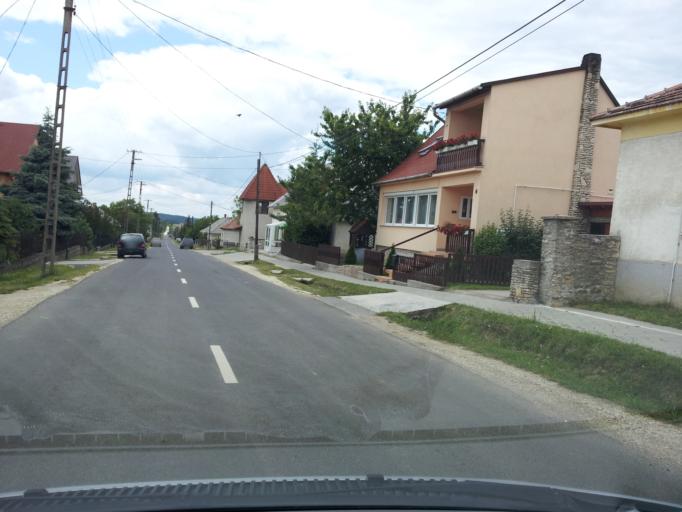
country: HU
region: Veszprem
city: Herend
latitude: 47.1850
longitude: 17.8121
